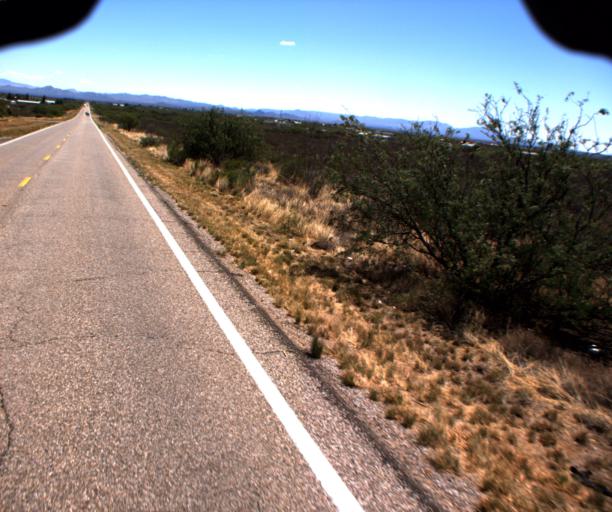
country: US
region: Arizona
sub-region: Cochise County
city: Huachuca City
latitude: 31.6920
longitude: -110.3838
